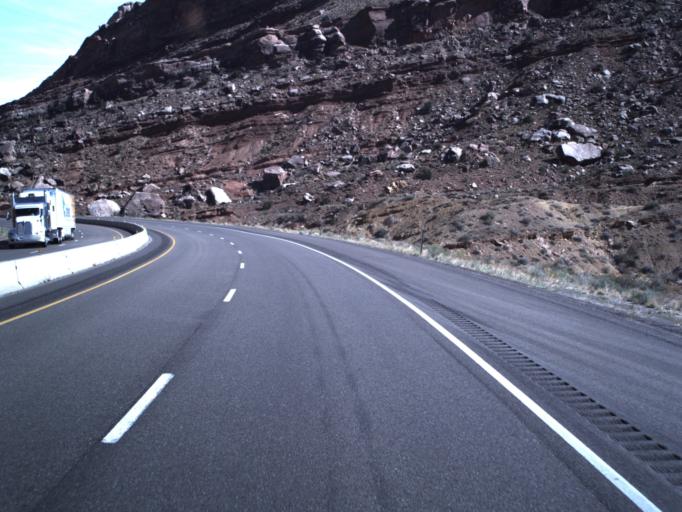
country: US
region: Utah
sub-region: Carbon County
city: East Carbon City
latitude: 38.9252
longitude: -110.4529
